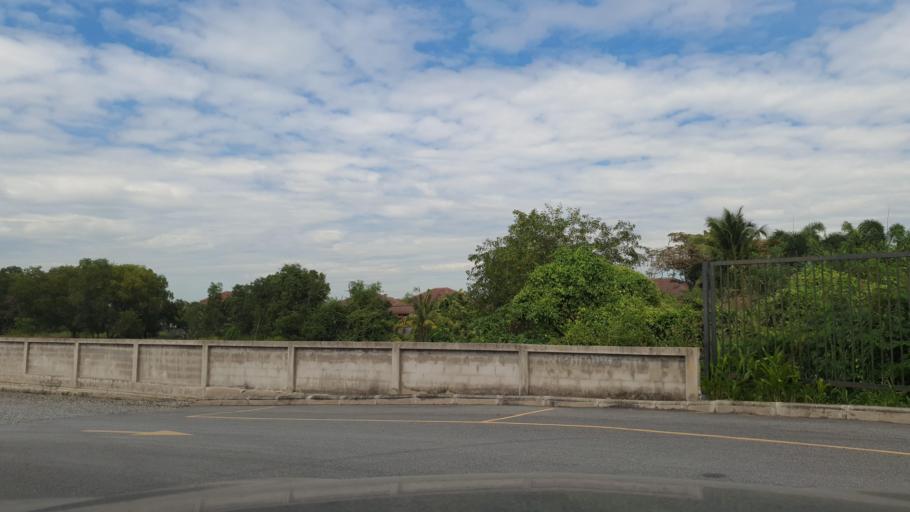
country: TH
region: Chon Buri
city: Phatthaya
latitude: 12.9510
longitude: 100.9367
